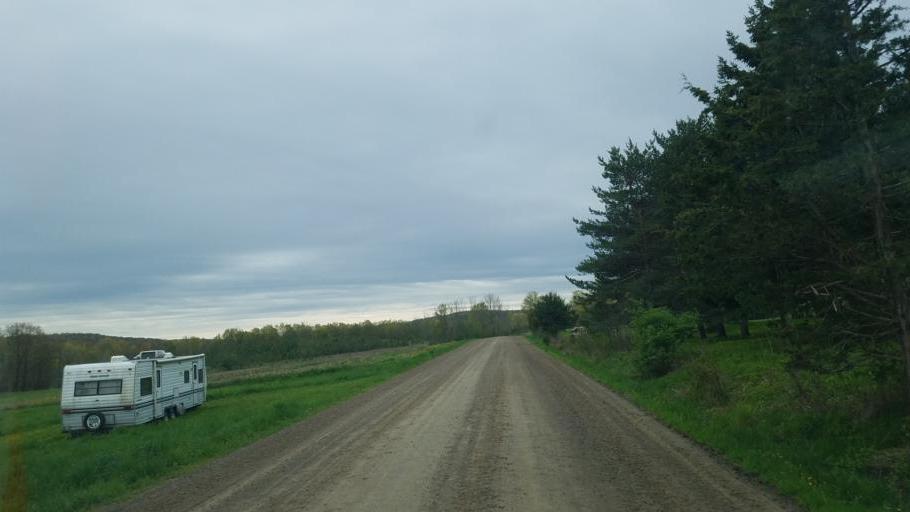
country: US
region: Pennsylvania
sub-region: Tioga County
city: Westfield
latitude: 42.0609
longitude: -77.4633
